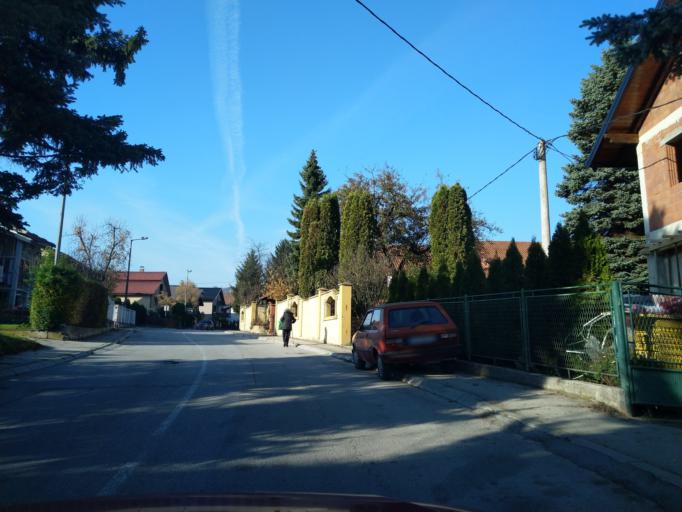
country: RS
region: Central Serbia
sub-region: Zlatiborski Okrug
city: Uzice
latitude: 43.8431
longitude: 19.8986
